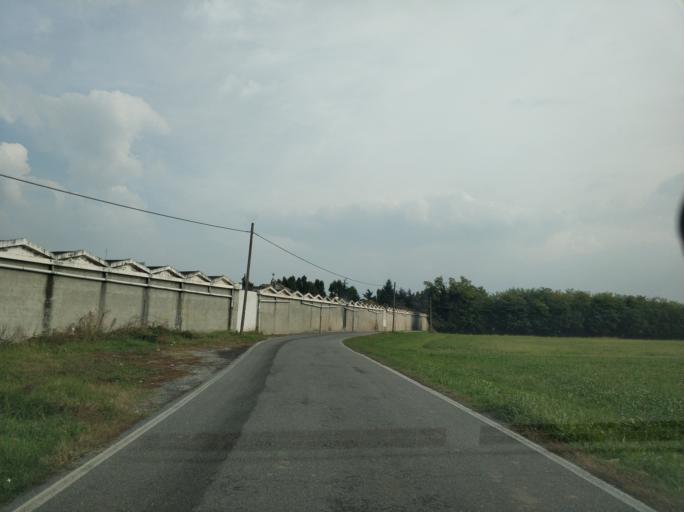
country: IT
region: Piedmont
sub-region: Provincia di Torino
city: San Carlo Canavese
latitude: 45.2412
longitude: 7.5980
